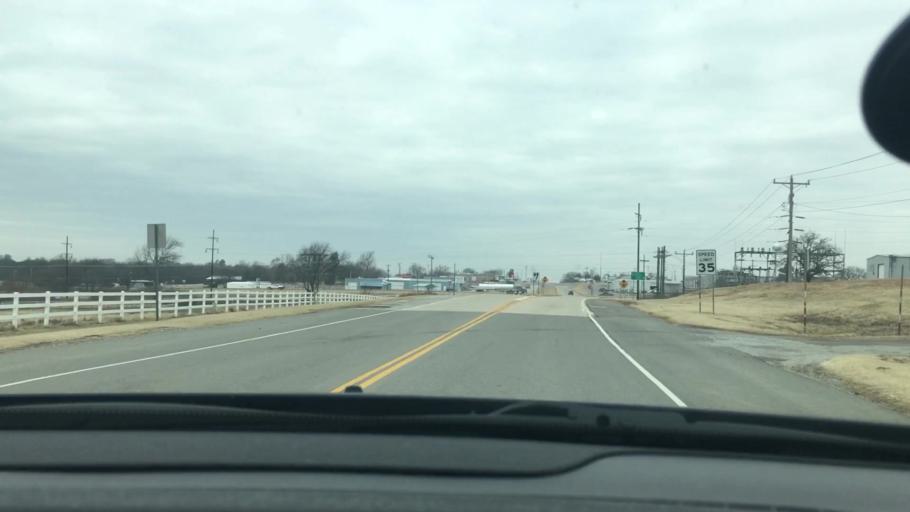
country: US
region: Oklahoma
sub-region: Carter County
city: Healdton
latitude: 34.4488
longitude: -97.5061
